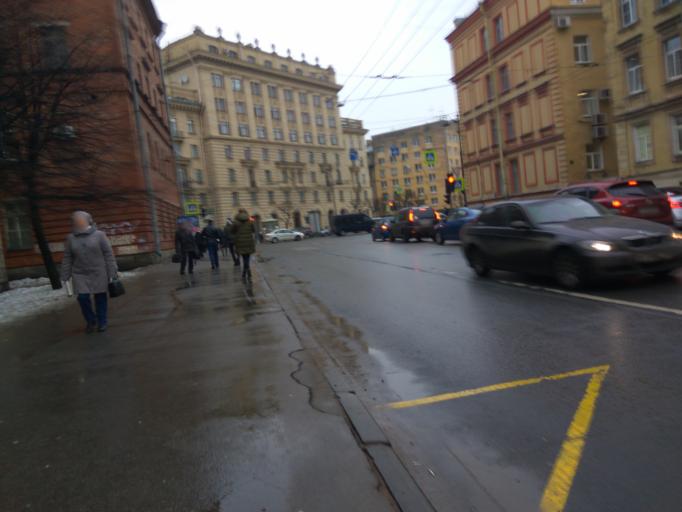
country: RU
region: St.-Petersburg
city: Centralniy
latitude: 59.9443
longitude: 30.3879
